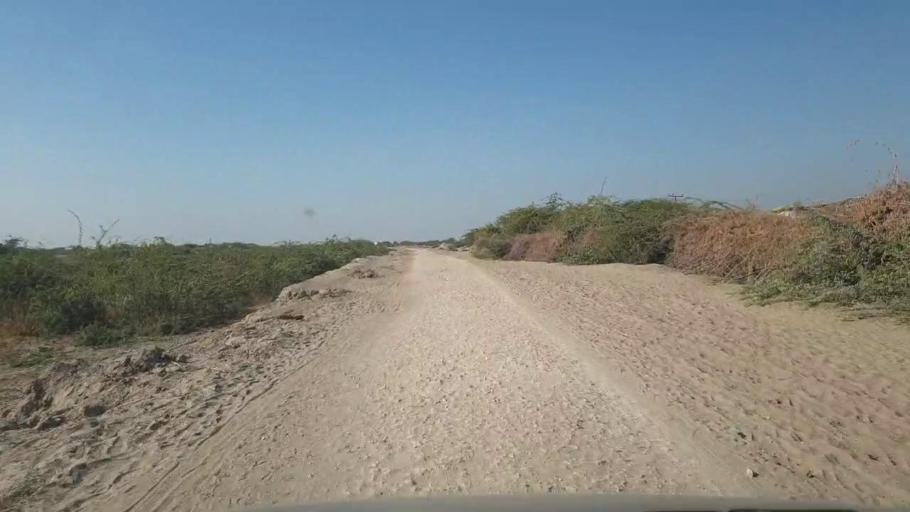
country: PK
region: Sindh
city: Pithoro
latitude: 25.4009
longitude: 69.2604
